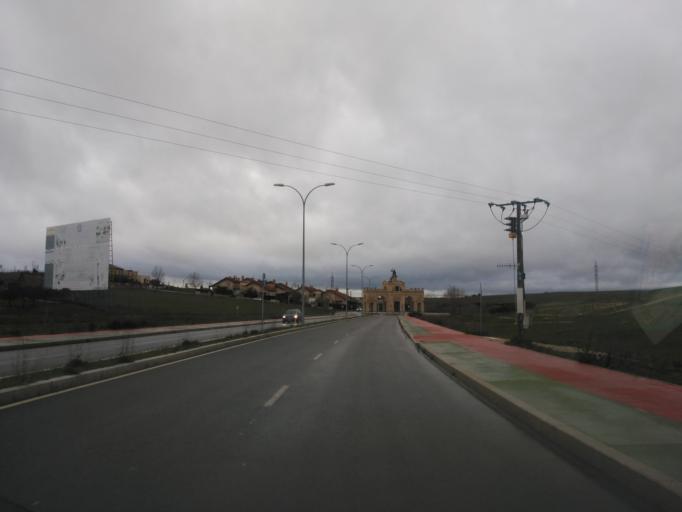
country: ES
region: Castille and Leon
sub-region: Provincia de Salamanca
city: Villamayor
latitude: 40.9806
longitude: -5.6928
